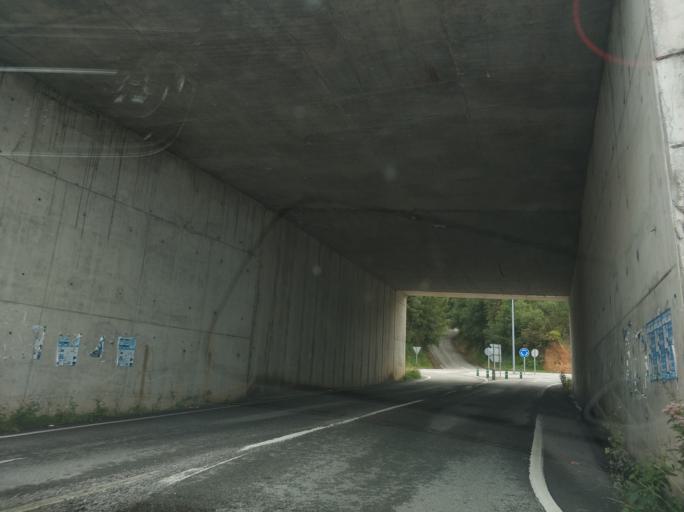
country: ES
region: Asturias
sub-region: Province of Asturias
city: Cudillero
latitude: 43.5572
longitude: -6.2835
